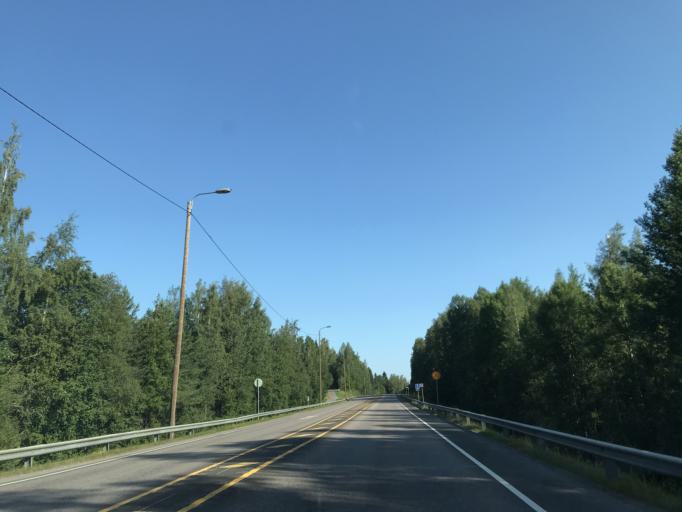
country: FI
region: Paijanne Tavastia
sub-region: Lahti
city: Lahti
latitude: 61.0398
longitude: 25.6670
